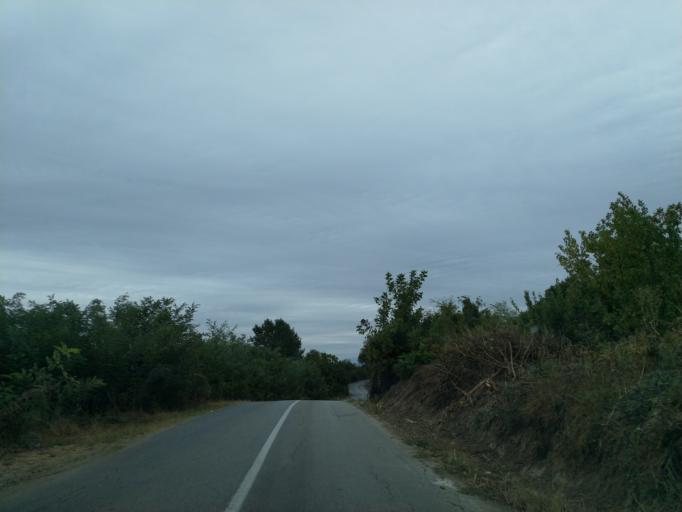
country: RS
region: Central Serbia
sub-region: Pomoravski Okrug
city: Cuprija
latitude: 43.8595
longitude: 21.3246
